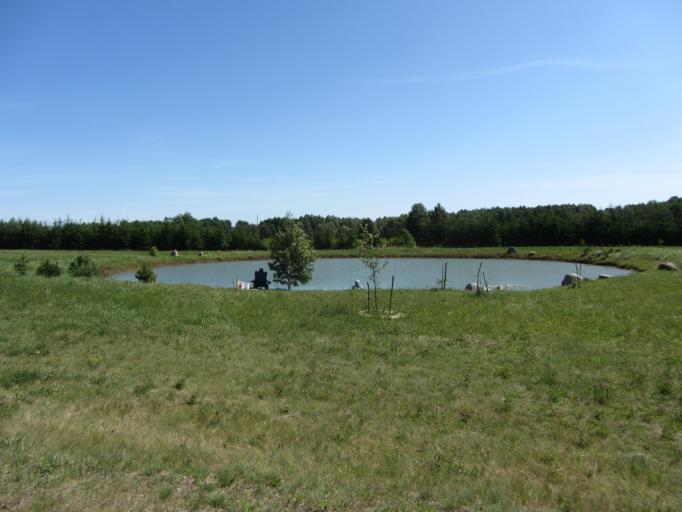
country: LT
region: Vilnius County
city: Elektrenai
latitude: 54.8393
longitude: 24.5666
